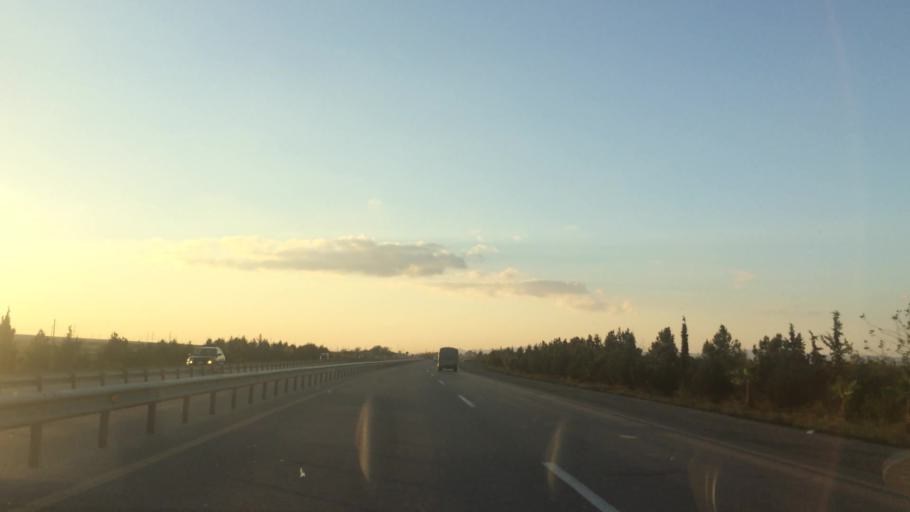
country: AZ
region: Haciqabul
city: Haciqabul
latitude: 40.0239
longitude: 49.1154
